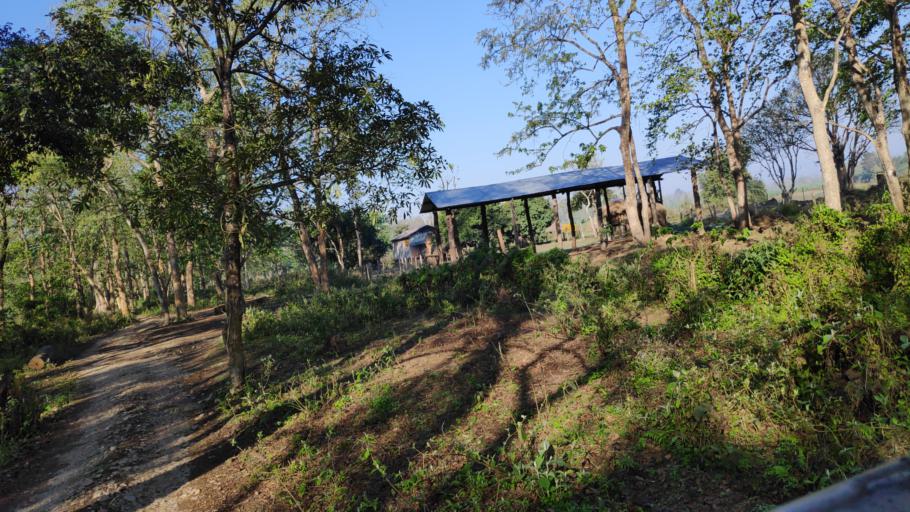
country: NP
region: Central Region
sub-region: Narayani Zone
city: Bharatpur
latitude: 27.5589
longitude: 84.5590
